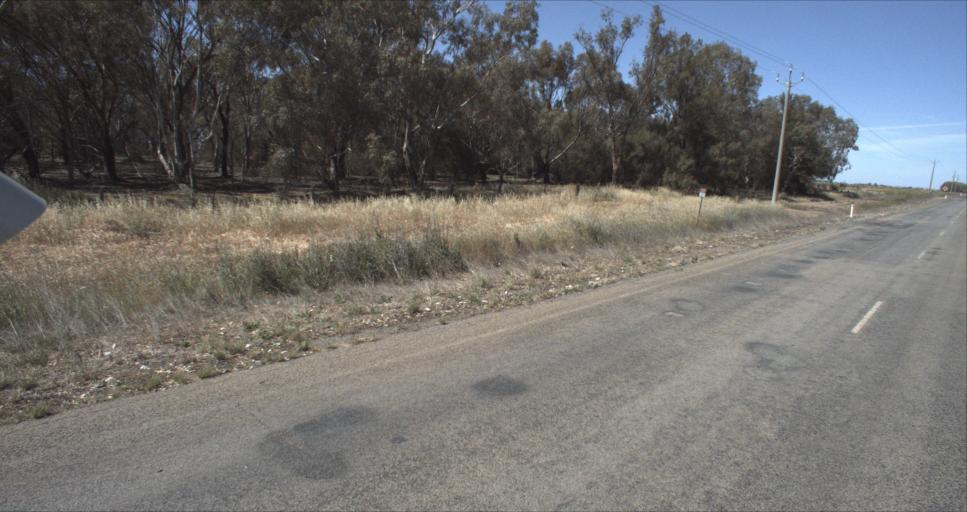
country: AU
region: New South Wales
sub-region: Leeton
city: Leeton
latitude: -34.4700
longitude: 146.2925
